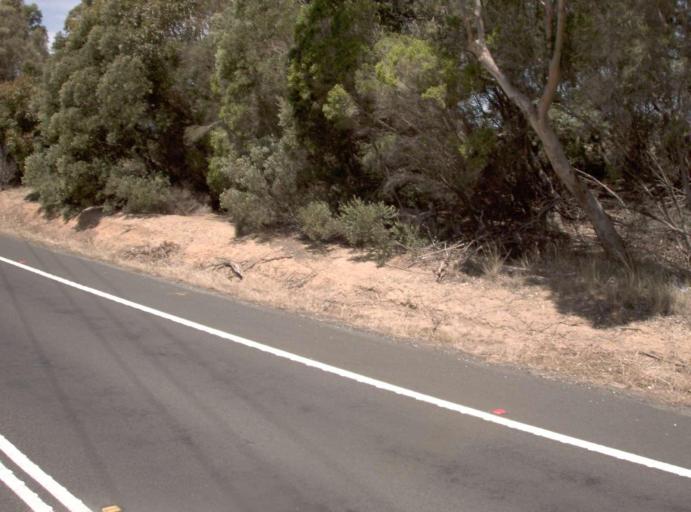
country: AU
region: Victoria
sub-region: Wellington
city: Heyfield
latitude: -38.1069
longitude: 146.8988
